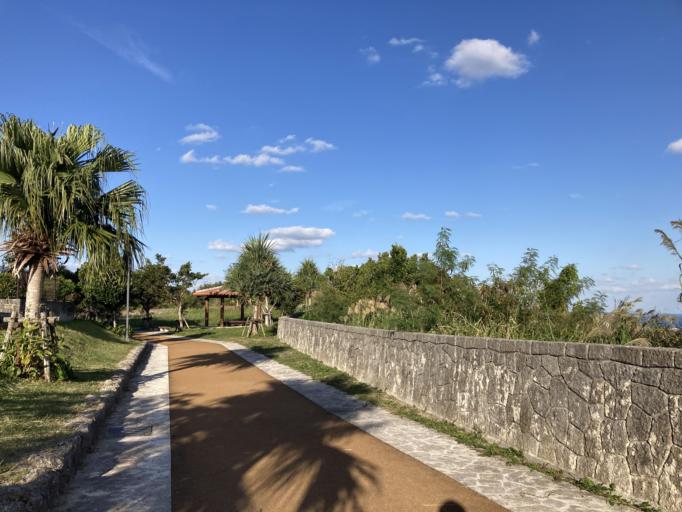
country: JP
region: Okinawa
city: Ginowan
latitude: 26.2557
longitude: 127.7775
